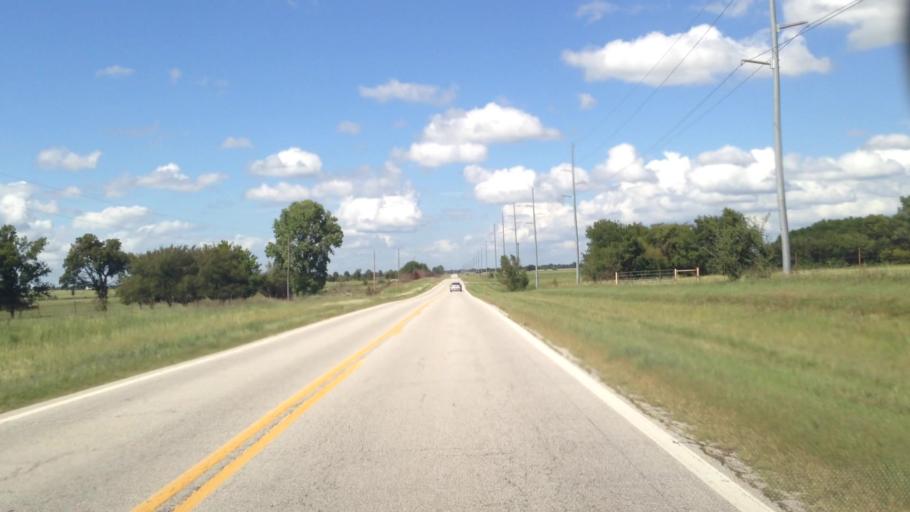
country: US
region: Kansas
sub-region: Labette County
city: Chetopa
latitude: 36.9548
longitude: -95.0832
